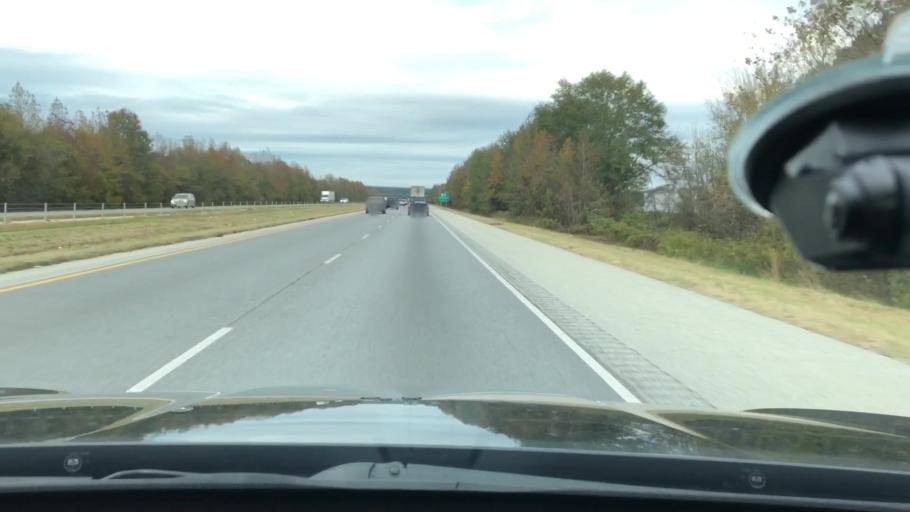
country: US
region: Arkansas
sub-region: Clark County
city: Arkadelphia
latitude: 34.1644
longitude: -93.0761
